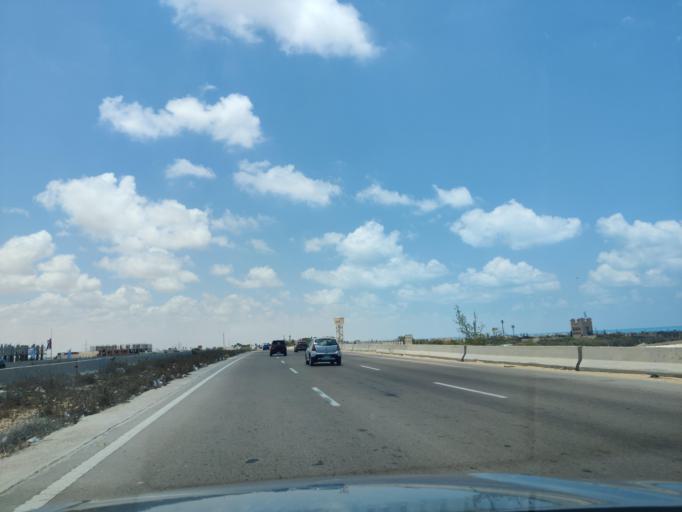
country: EG
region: Muhafazat Matruh
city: Al `Alamayn
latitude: 30.8323
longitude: 29.2235
